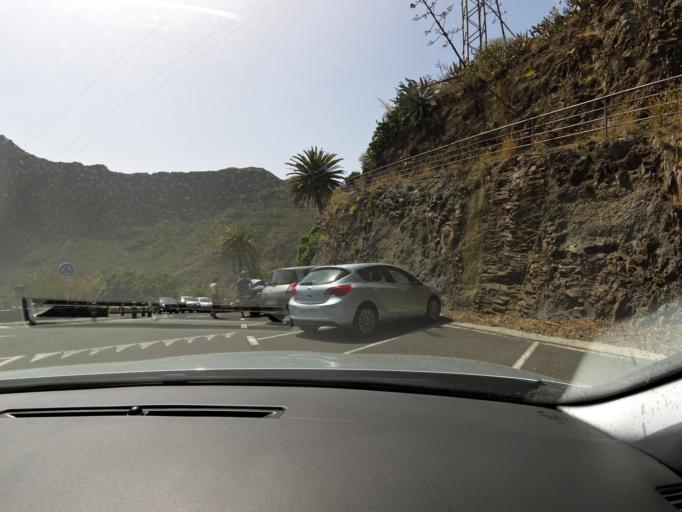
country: ES
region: Canary Islands
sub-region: Provincia de Santa Cruz de Tenerife
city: Santiago del Teide
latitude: 28.3053
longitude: -16.8399
